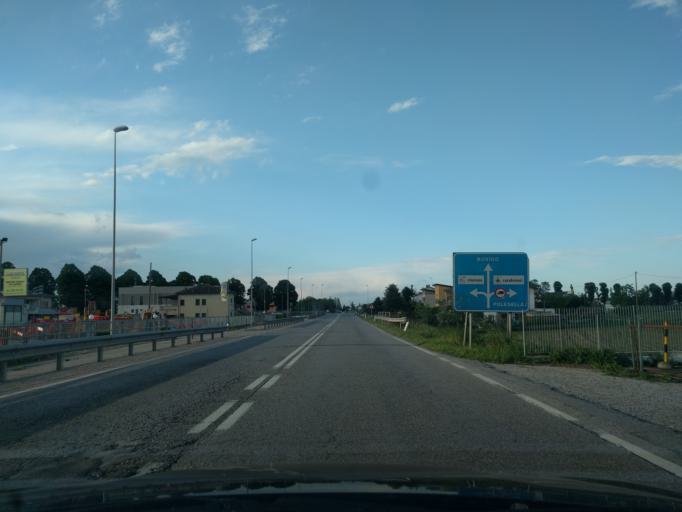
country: IT
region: Veneto
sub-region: Provincia di Rovigo
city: Polesella
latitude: 44.9591
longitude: 11.7401
